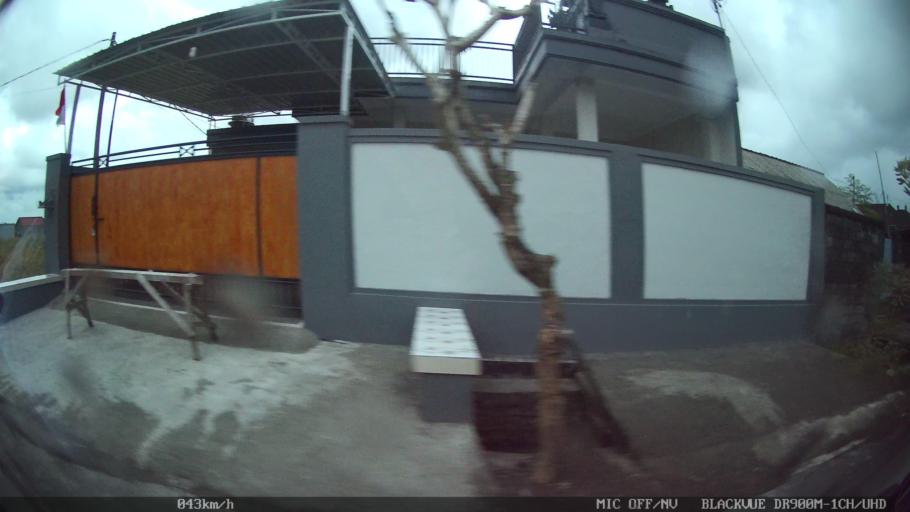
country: ID
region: Bali
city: Banjar Cemenggon
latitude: -8.5291
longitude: 115.1893
